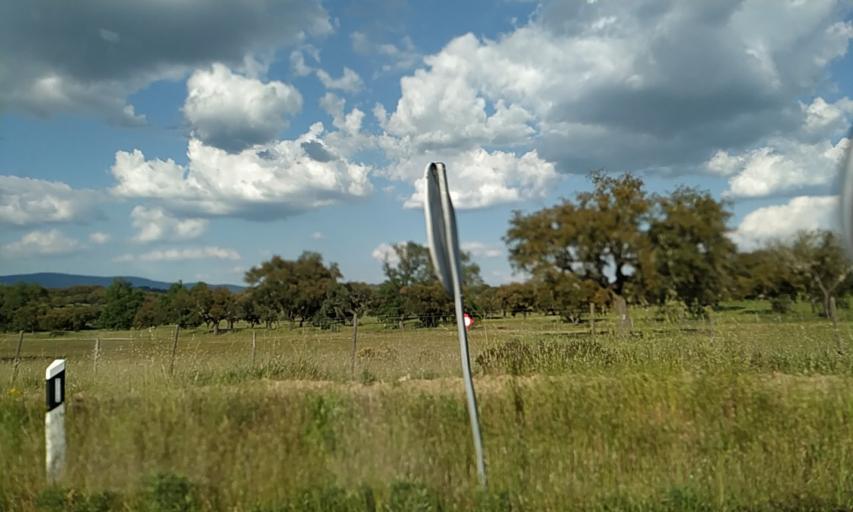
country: PT
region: Portalegre
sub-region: Portalegre
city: Urra
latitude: 39.2132
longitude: -7.4585
